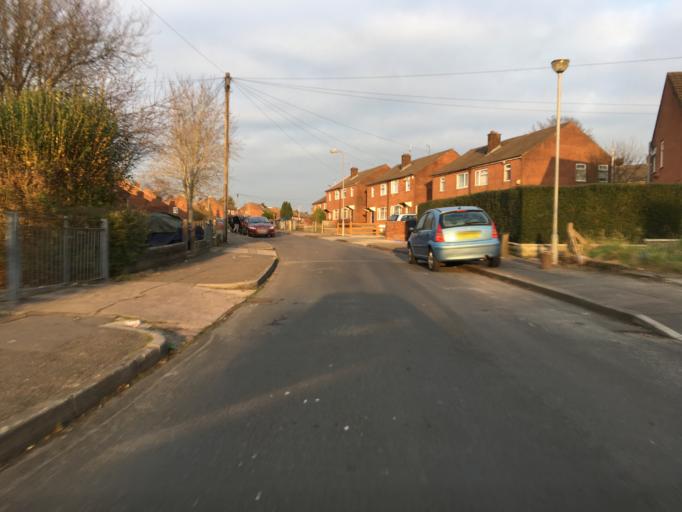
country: GB
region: Wales
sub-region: Newport
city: Marshfield
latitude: 51.5253
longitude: -3.1226
